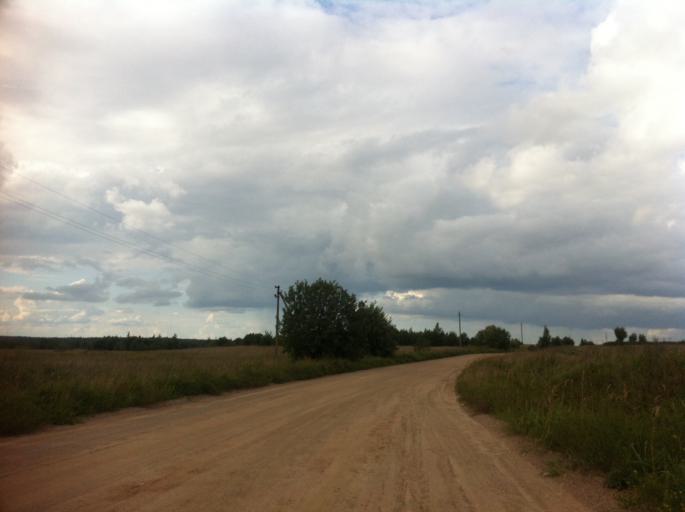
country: RU
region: Pskov
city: Izborsk
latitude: 57.8197
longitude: 27.9780
